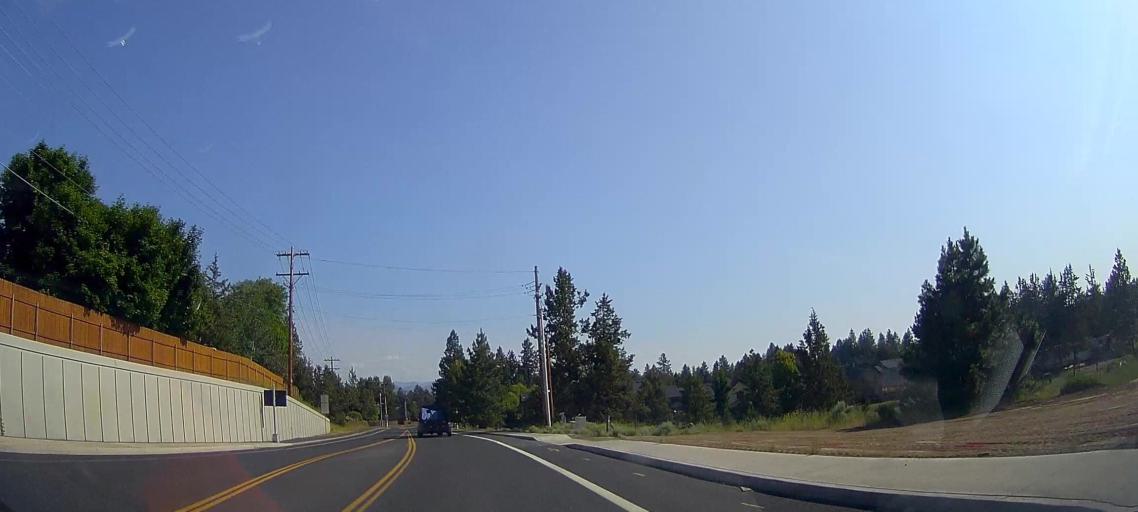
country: US
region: Oregon
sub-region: Deschutes County
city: Bend
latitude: 44.0361
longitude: -121.2839
